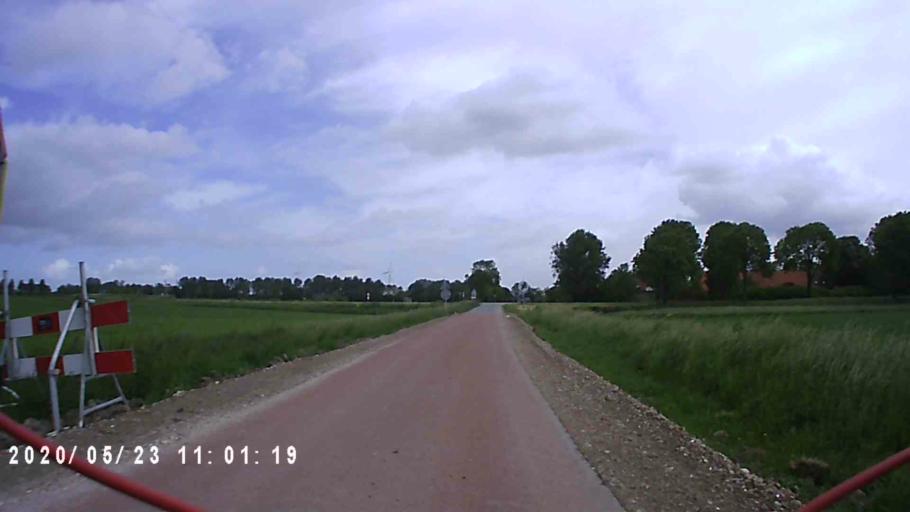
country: NL
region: Groningen
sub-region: Gemeente Delfzijl
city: Delfzijl
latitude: 53.3087
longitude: 6.9438
